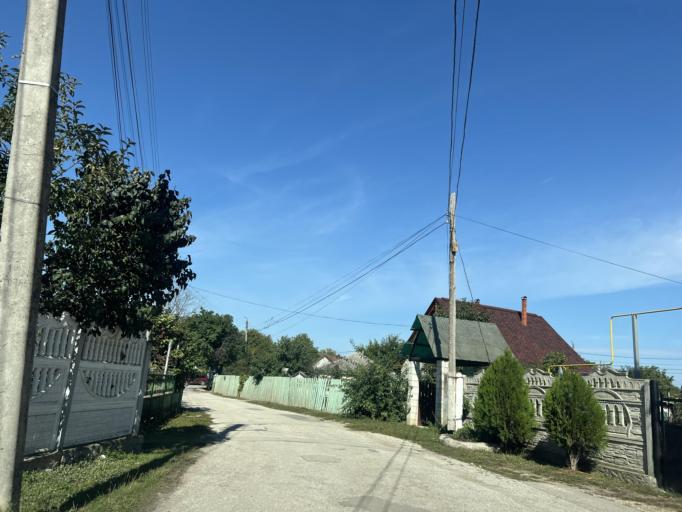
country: RO
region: Iasi
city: Ungheni-Prut
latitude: 47.1940
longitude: 27.7890
